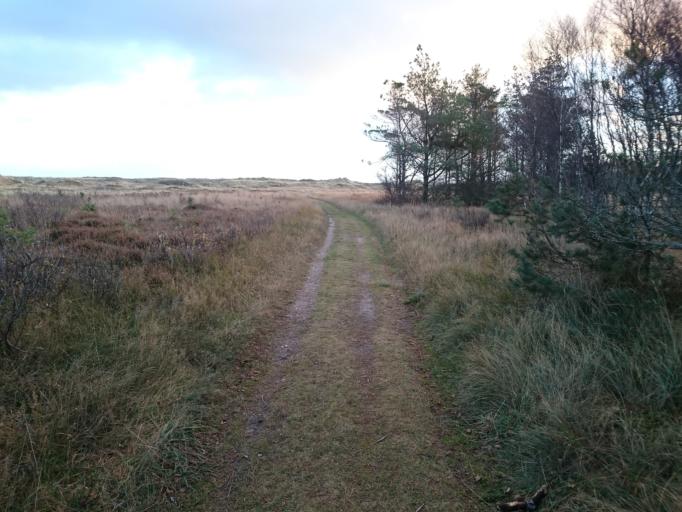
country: DK
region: North Denmark
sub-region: Frederikshavn Kommune
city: Skagen
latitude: 57.7018
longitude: 10.5427
